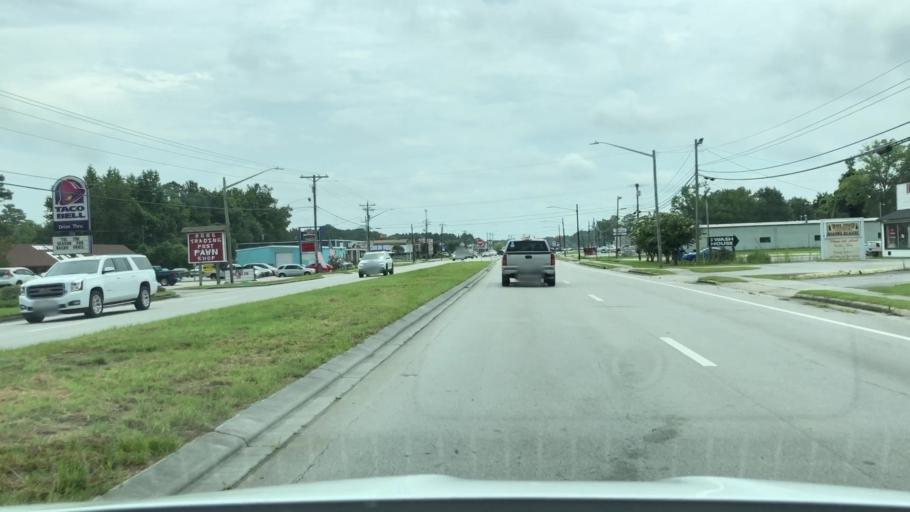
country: US
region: North Carolina
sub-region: Craven County
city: Havelock
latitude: 34.8680
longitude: -76.9002
